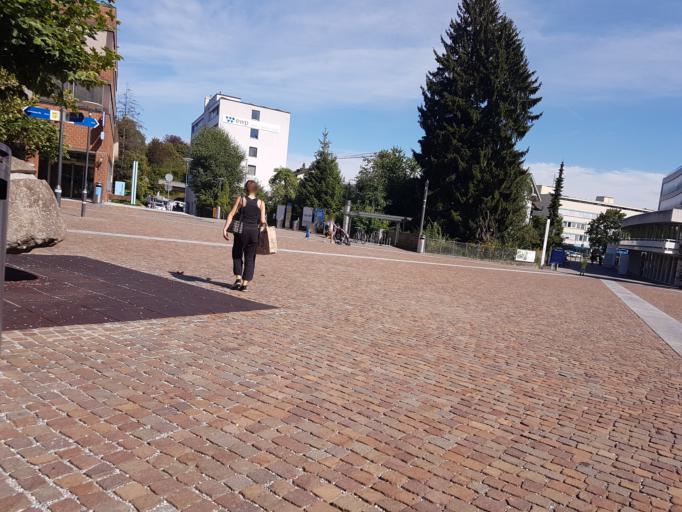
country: CH
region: Zurich
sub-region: Bezirk Pfaeffikon
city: Effretikon
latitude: 47.4282
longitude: 8.6855
